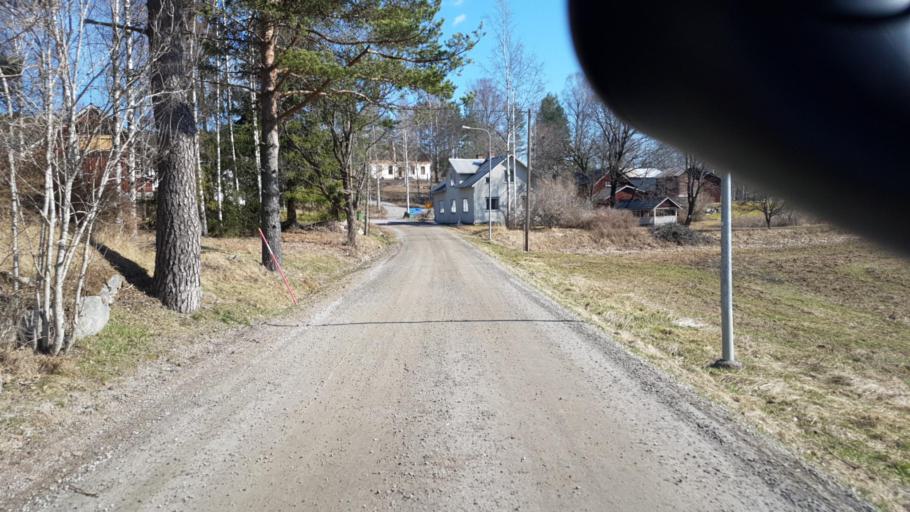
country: SE
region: Vaermland
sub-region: Arvika Kommun
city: Arvika
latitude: 59.6878
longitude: 12.7855
